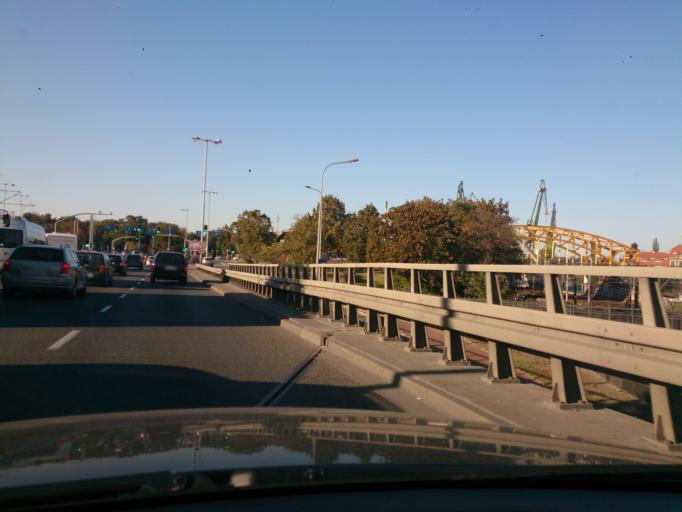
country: PL
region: Pomeranian Voivodeship
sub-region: Gdansk
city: Gdansk
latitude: 54.3604
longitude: 18.6438
